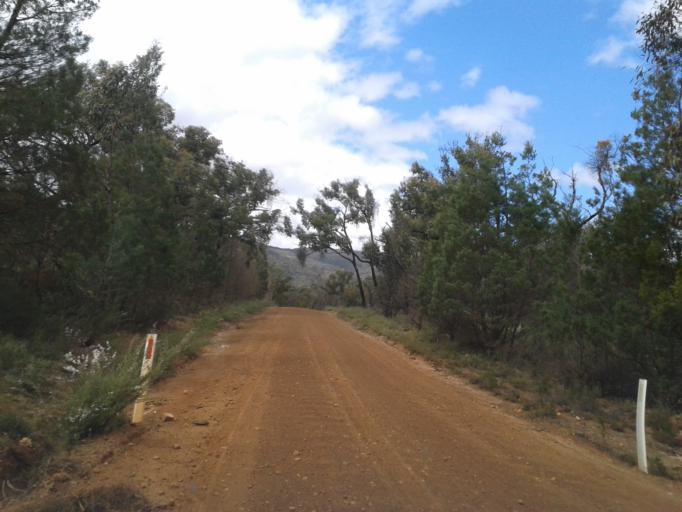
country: AU
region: Victoria
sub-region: Horsham
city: Horsham
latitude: -37.2521
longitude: 142.2619
